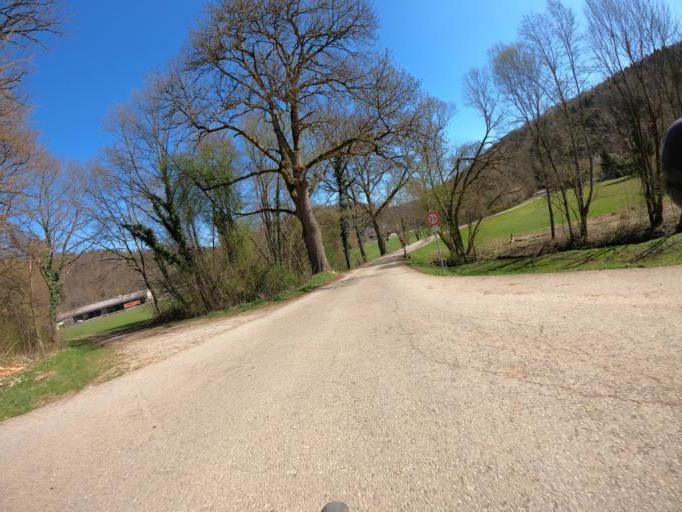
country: DE
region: Baden-Wuerttemberg
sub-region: Tuebingen Region
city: Haigerloch
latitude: 48.4043
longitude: 8.7669
